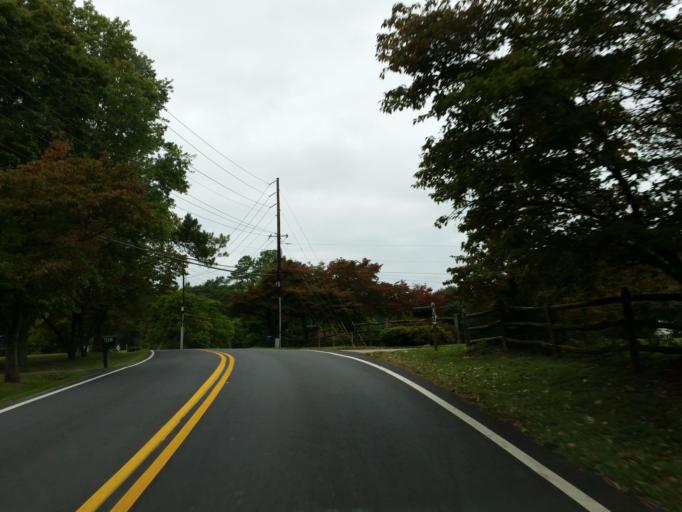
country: US
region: Georgia
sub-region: Cherokee County
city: Woodstock
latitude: 34.0493
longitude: -84.5233
